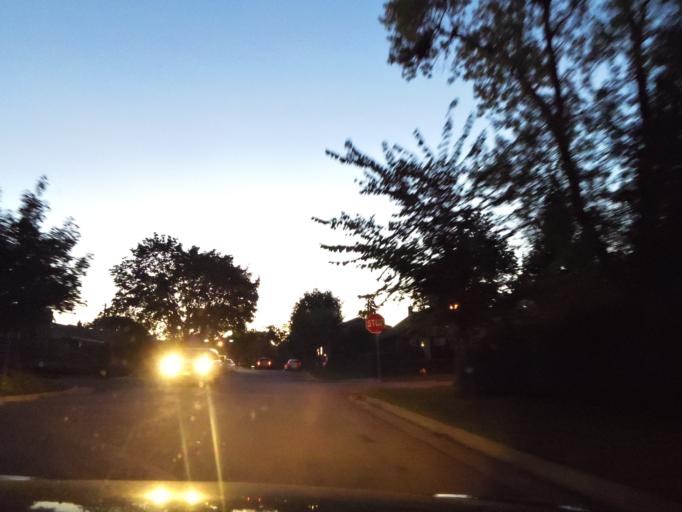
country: US
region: Minnesota
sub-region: Dakota County
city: Mendota Heights
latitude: 44.9234
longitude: -93.1653
